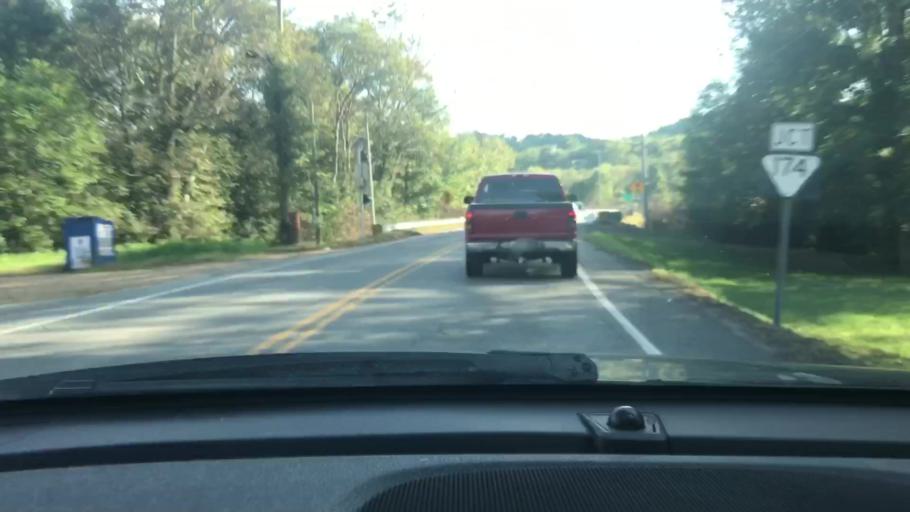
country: US
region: Tennessee
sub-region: Sumner County
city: Shackle Island
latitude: 36.3730
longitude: -86.6170
